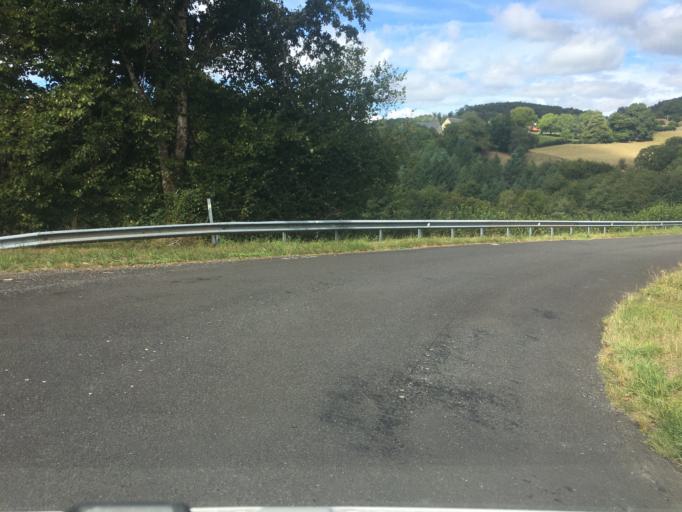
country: FR
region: Auvergne
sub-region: Departement du Cantal
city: Champagnac
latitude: 45.4393
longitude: 2.4016
